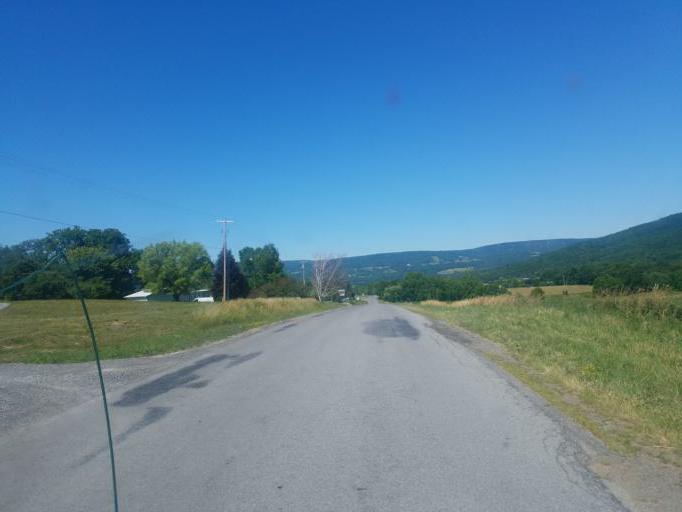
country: US
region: New York
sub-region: Ontario County
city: Canandaigua
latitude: 42.7257
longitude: -77.2877
